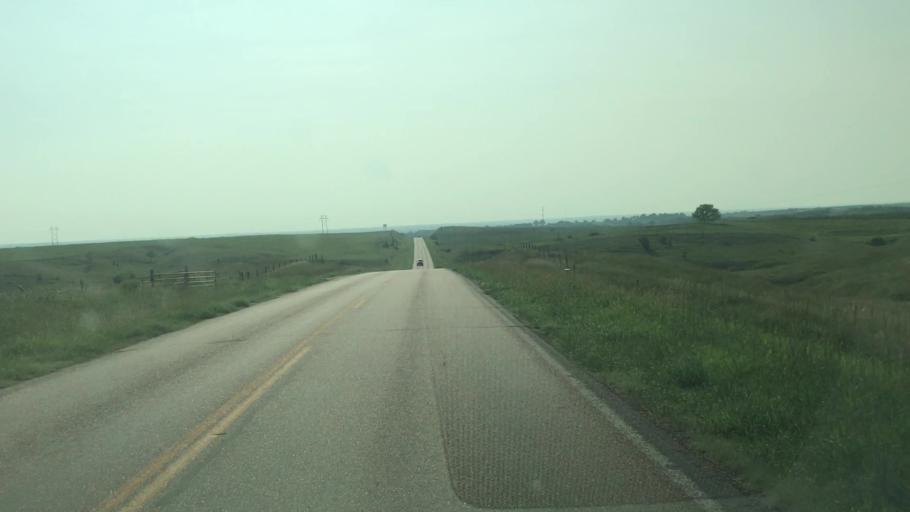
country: US
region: Nebraska
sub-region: Sherman County
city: Loup City
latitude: 41.2793
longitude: -98.9343
